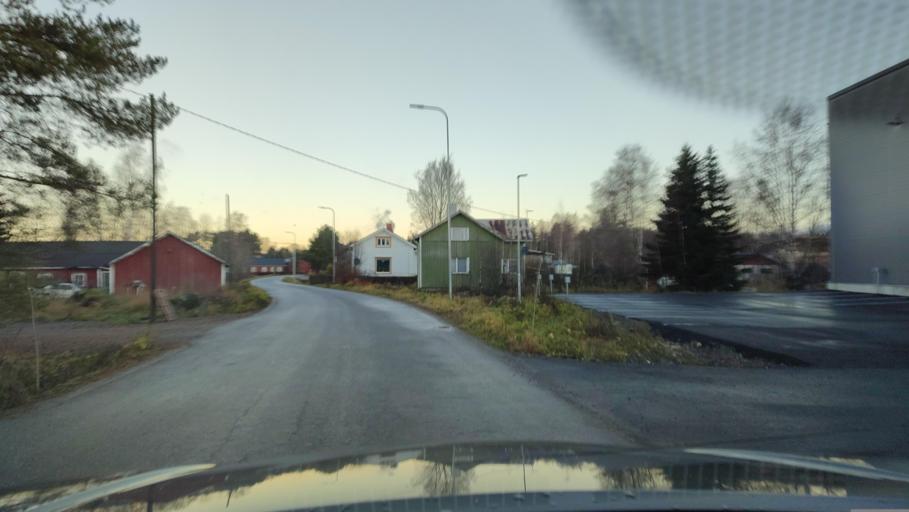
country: FI
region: Ostrobothnia
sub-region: Sydosterbotten
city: Naerpes
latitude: 62.4753
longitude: 21.3584
